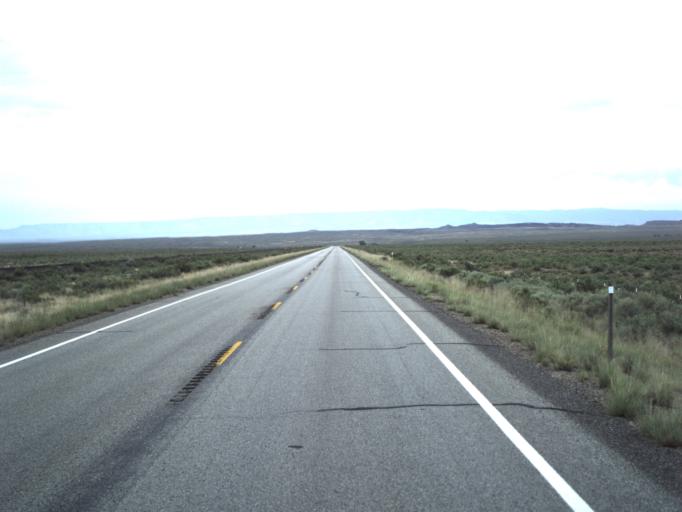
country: US
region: Utah
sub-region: Carbon County
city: East Carbon City
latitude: 39.5333
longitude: -110.5315
